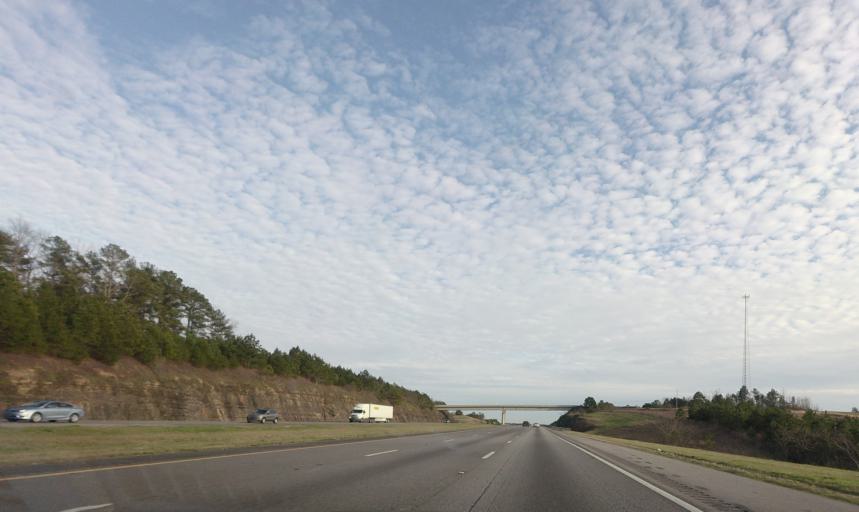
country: US
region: Alabama
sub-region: Walker County
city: Dora
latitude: 33.6941
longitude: -87.1252
